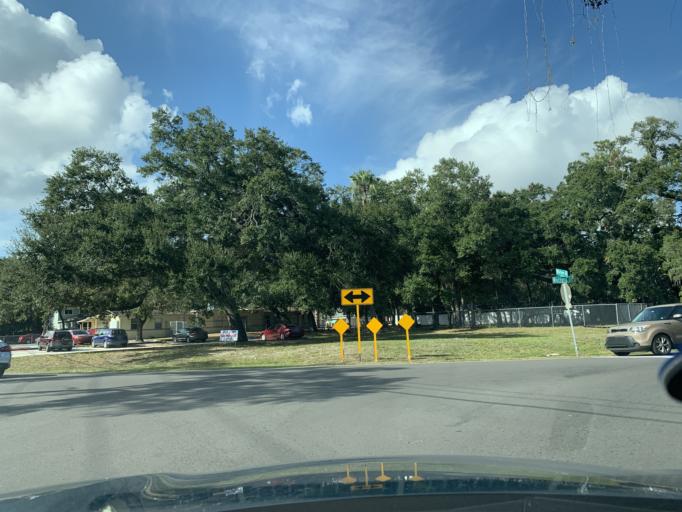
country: US
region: Florida
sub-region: Pinellas County
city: South Highpoint
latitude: 27.9237
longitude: -82.7178
